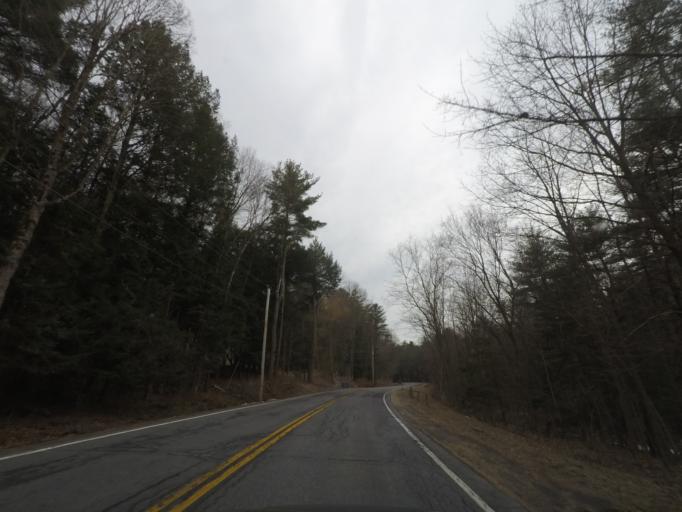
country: US
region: New York
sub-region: Washington County
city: Greenwich
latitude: 43.0496
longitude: -73.4953
